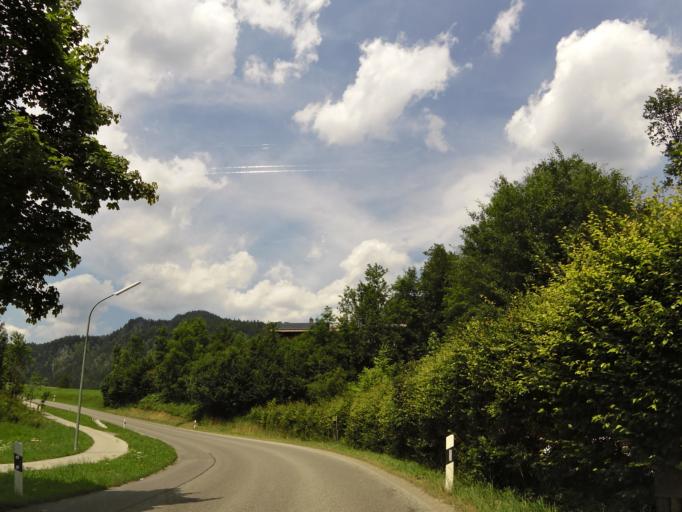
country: DE
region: Bavaria
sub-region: Upper Bavaria
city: Reit im Winkl
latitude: 47.6722
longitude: 12.4769
